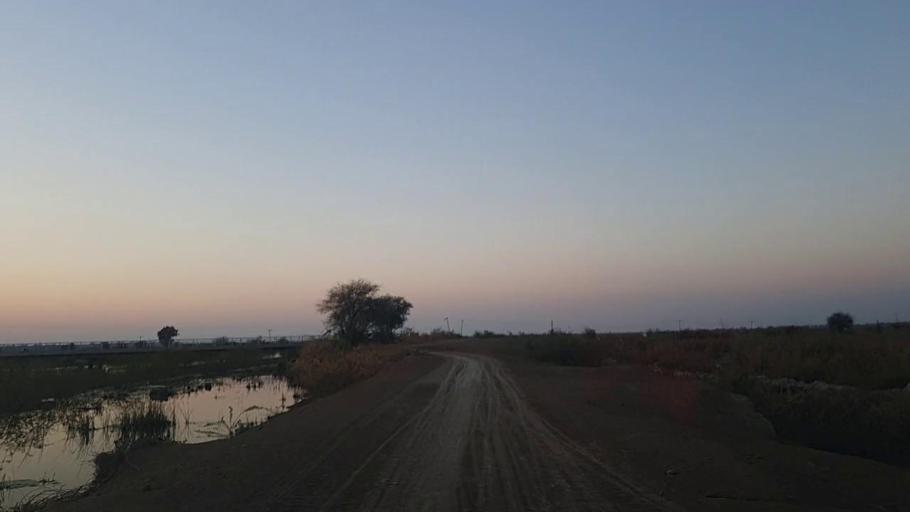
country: PK
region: Sindh
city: Tando Mittha Khan
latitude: 26.0668
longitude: 69.1603
